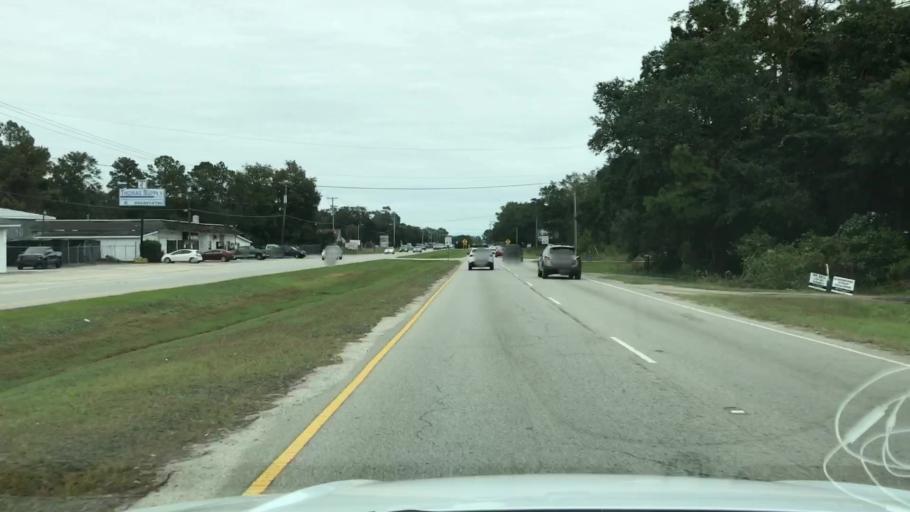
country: US
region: South Carolina
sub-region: Georgetown County
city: Murrells Inlet
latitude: 33.5455
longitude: -79.0511
